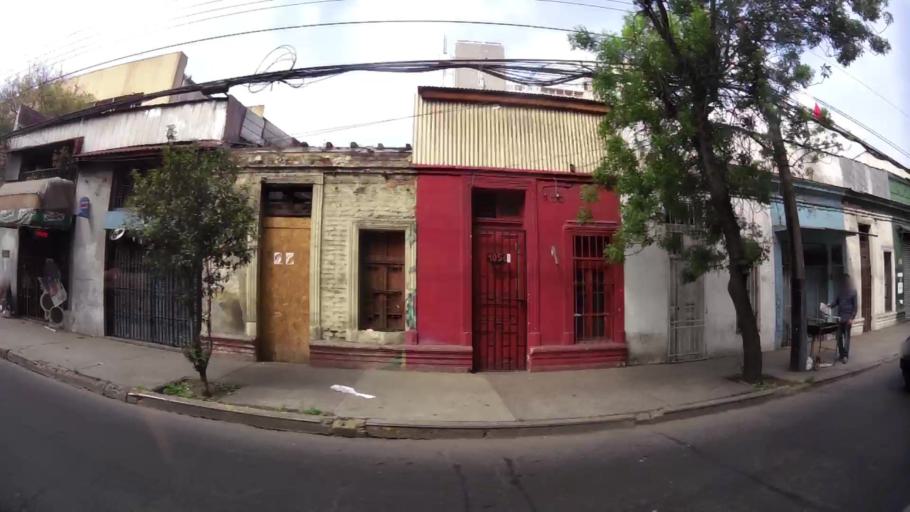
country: CL
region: Santiago Metropolitan
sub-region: Provincia de Santiago
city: Santiago
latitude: -33.4698
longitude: -70.6478
